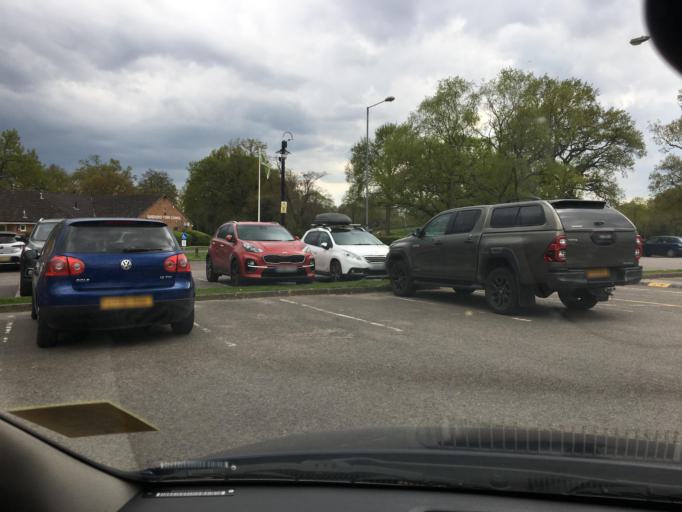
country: GB
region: England
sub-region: Bracknell Forest
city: Sandhurst
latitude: 51.3450
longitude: -0.7920
